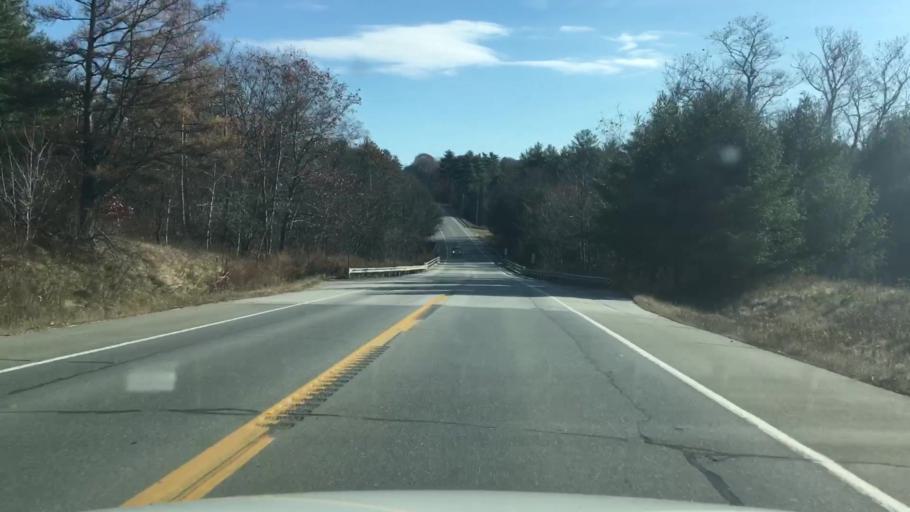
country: US
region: Maine
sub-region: Kennebec County
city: Windsor
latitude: 44.2588
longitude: -69.5546
